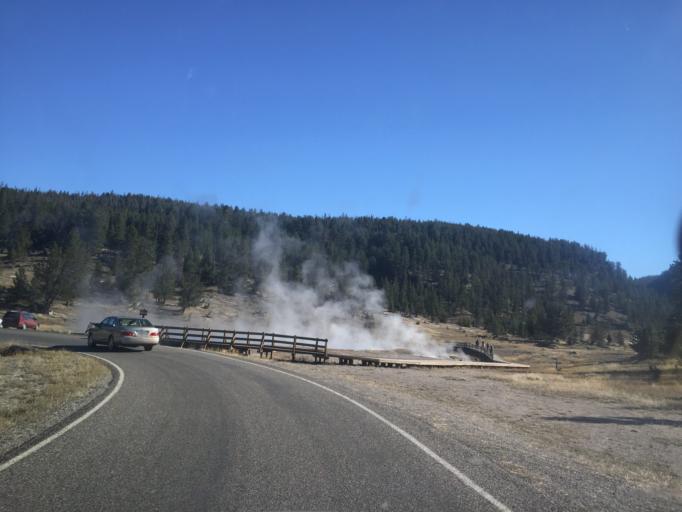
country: US
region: Montana
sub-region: Gallatin County
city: West Yellowstone
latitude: 44.5437
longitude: -110.7856
